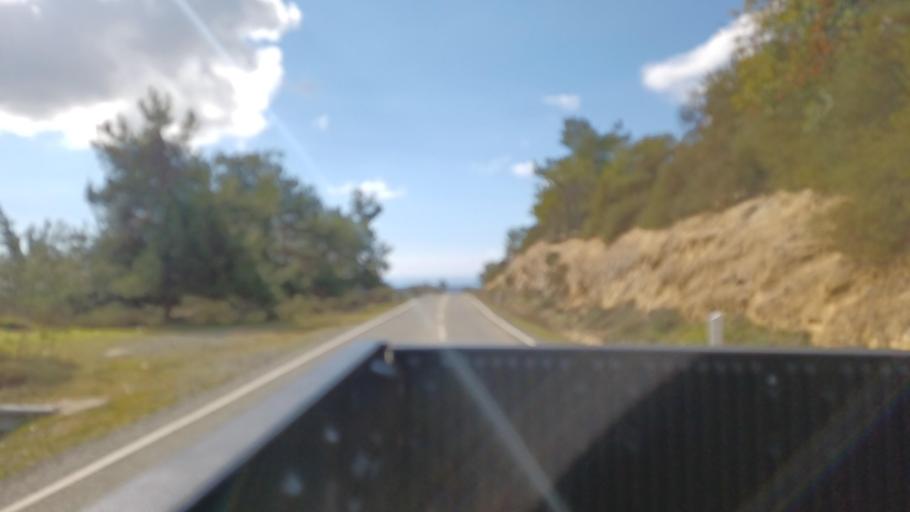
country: CY
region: Limassol
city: Pissouri
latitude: 34.7595
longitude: 32.6952
